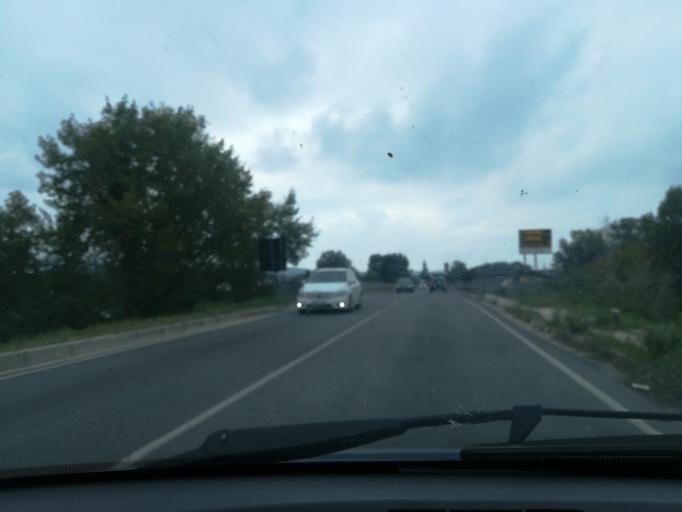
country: IT
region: The Marches
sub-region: Provincia di Macerata
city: Piediripa
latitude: 43.2733
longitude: 13.4854
